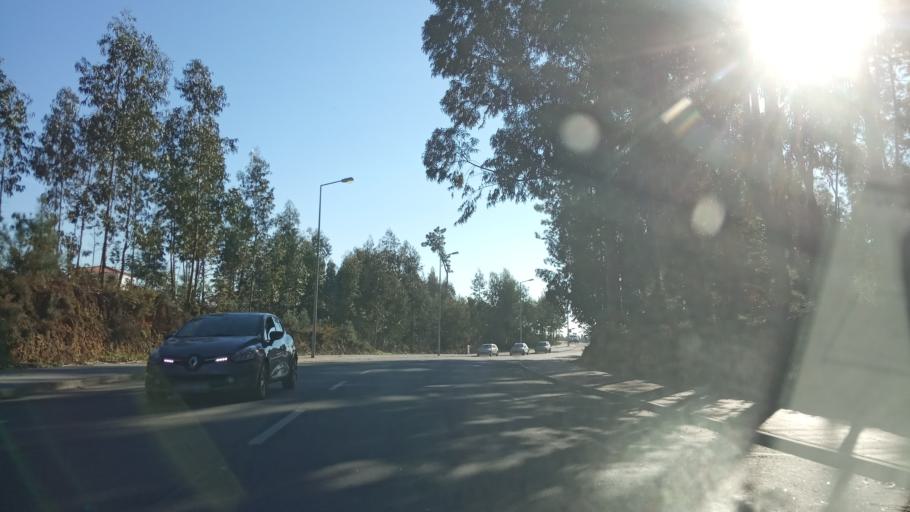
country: PT
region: Aveiro
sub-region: Anadia
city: Anadia
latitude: 40.4306
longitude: -8.4366
